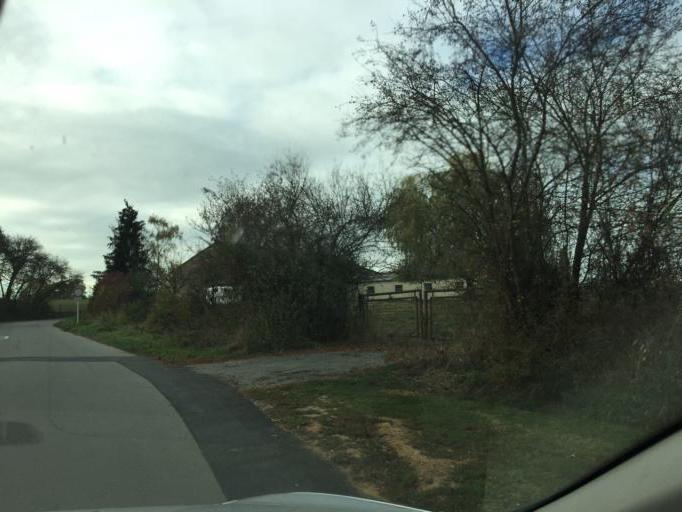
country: LU
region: Luxembourg
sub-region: Canton de Luxembourg
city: Bertrange
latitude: 49.6084
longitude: 6.0428
